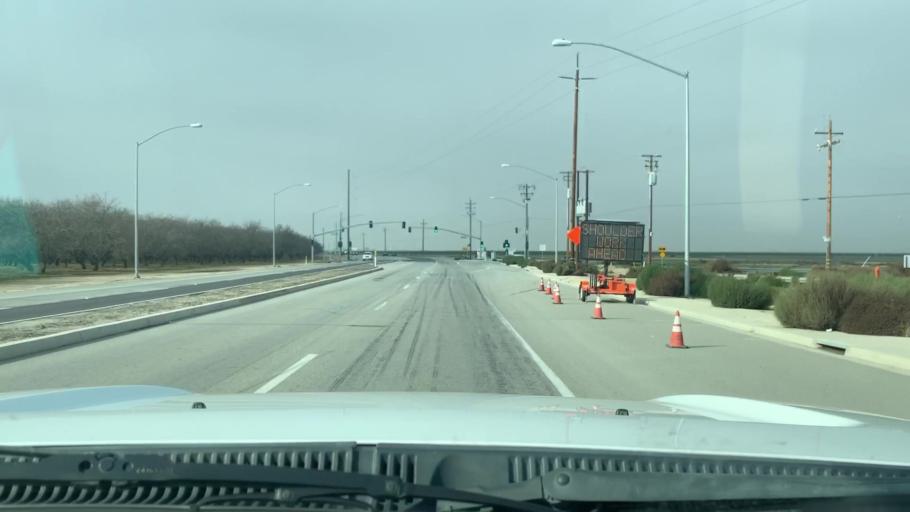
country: US
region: California
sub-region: Kern County
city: Rosedale
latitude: 35.4413
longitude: -119.2032
